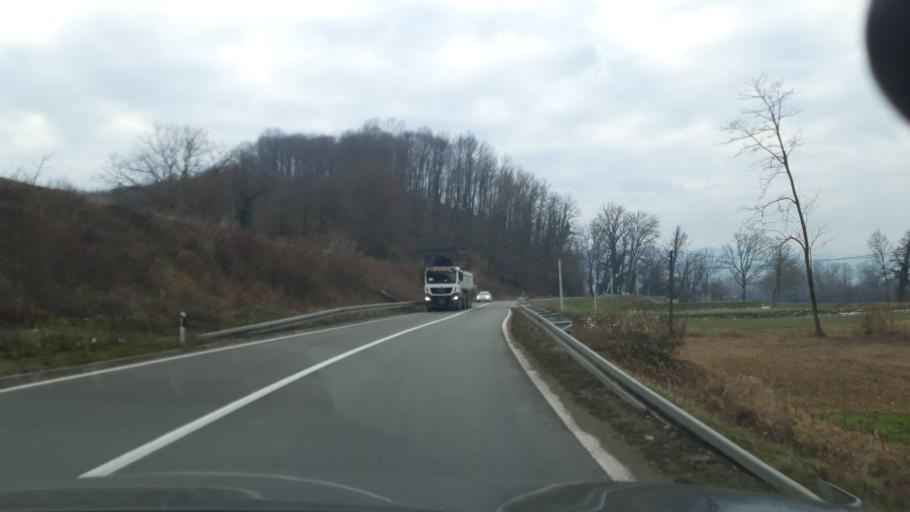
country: BA
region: Republika Srpska
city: Zvornik
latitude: 44.4225
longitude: 19.1498
